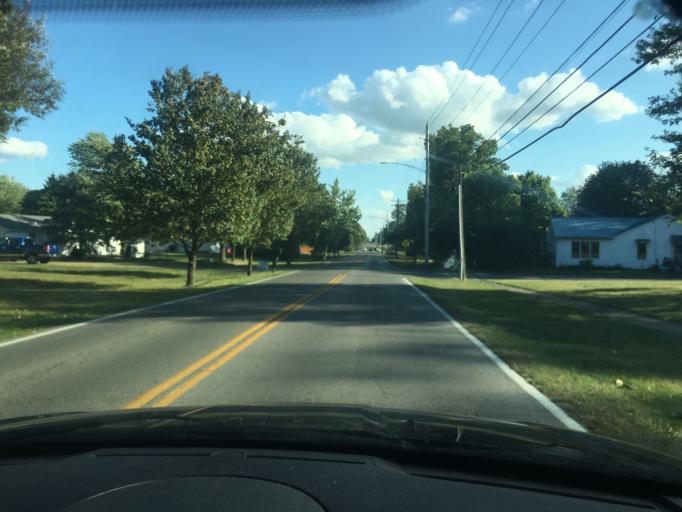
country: US
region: Ohio
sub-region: Logan County
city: Bellefontaine
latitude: 40.3539
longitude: -83.7515
